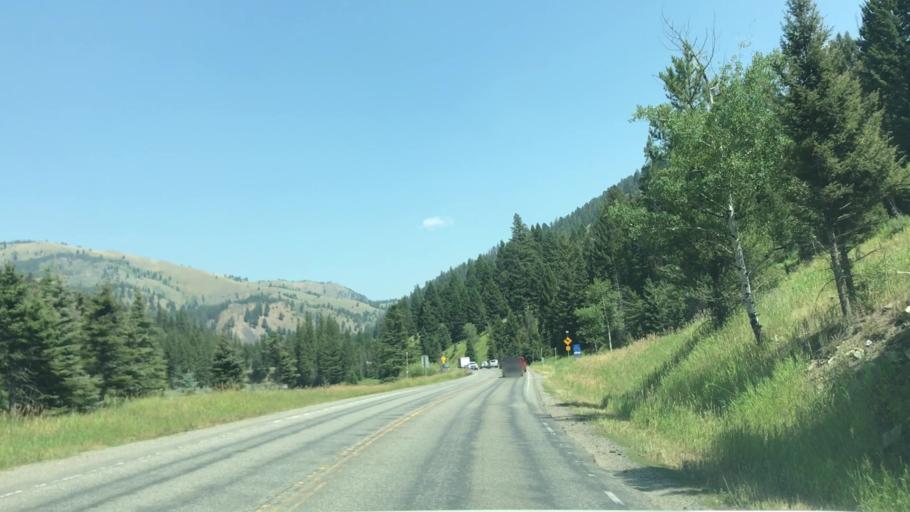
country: US
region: Montana
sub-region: Gallatin County
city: Big Sky
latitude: 45.2833
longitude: -111.2244
